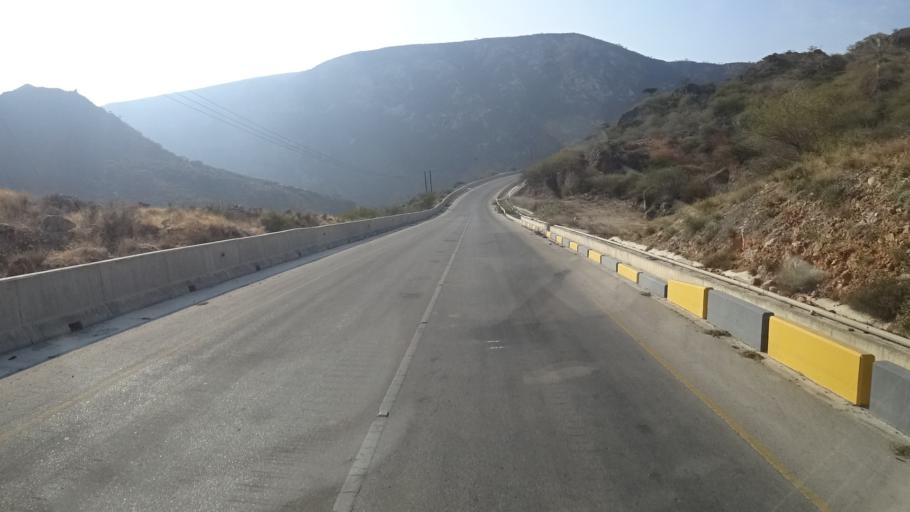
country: YE
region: Al Mahrah
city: Hawf
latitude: 16.7458
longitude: 53.2294
